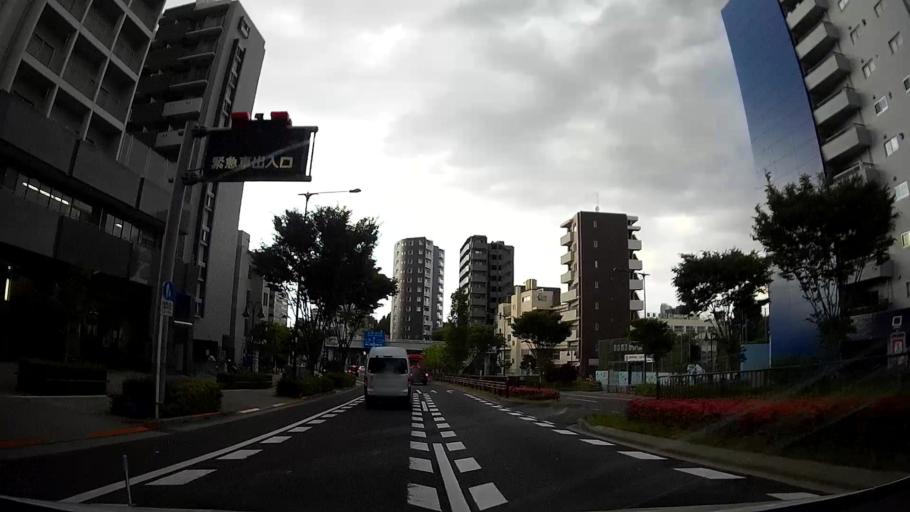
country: JP
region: Tokyo
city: Tokyo
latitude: 35.6997
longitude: 139.6830
